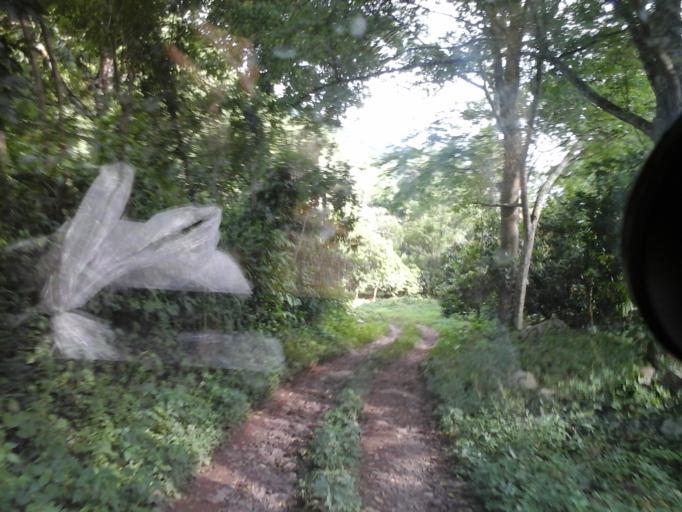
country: CO
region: Cesar
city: San Diego
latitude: 10.2827
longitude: -73.0887
